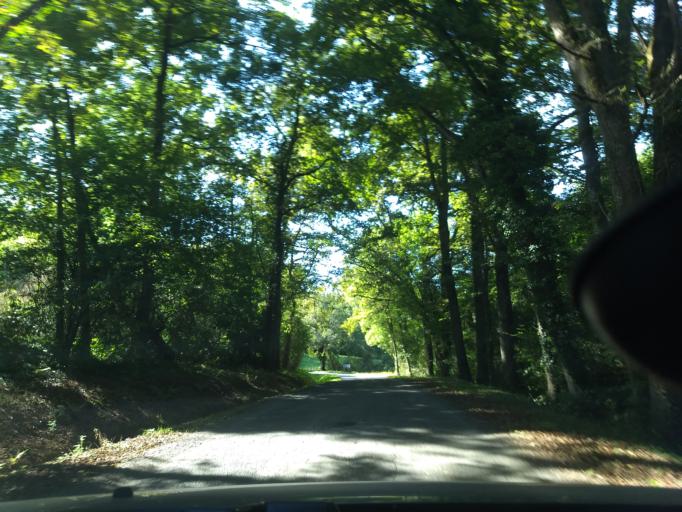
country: FR
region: Aquitaine
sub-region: Departement des Pyrenees-Atlantiques
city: Soumoulou
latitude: 43.2909
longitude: -0.1469
